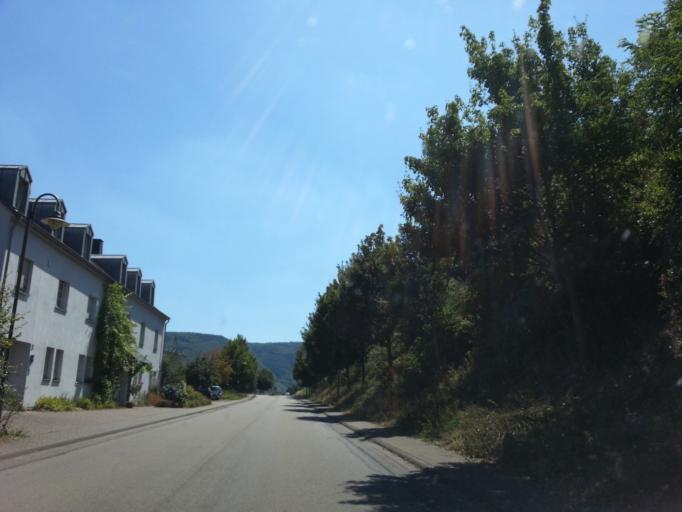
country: DE
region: Rheinland-Pfalz
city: Schleich
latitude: 49.8119
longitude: 6.8406
